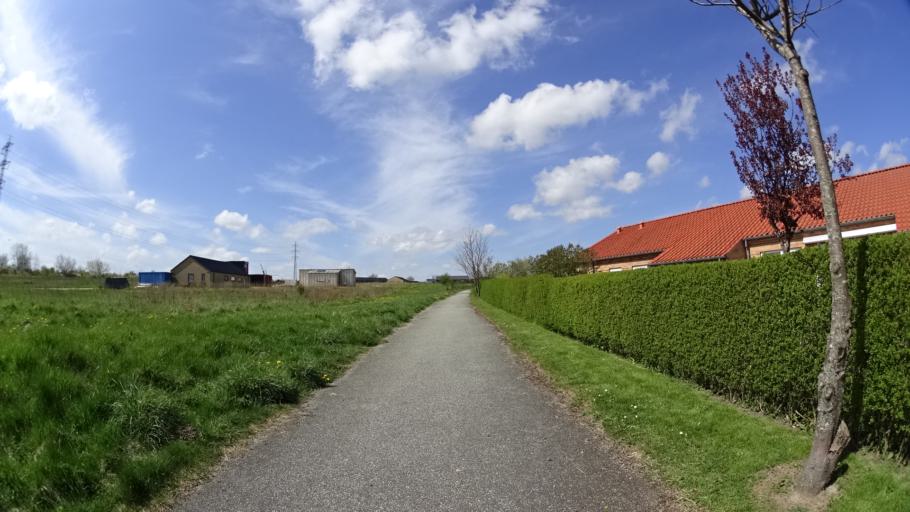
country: DK
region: Central Jutland
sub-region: Arhus Kommune
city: Stavtrup
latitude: 56.1264
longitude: 10.1150
